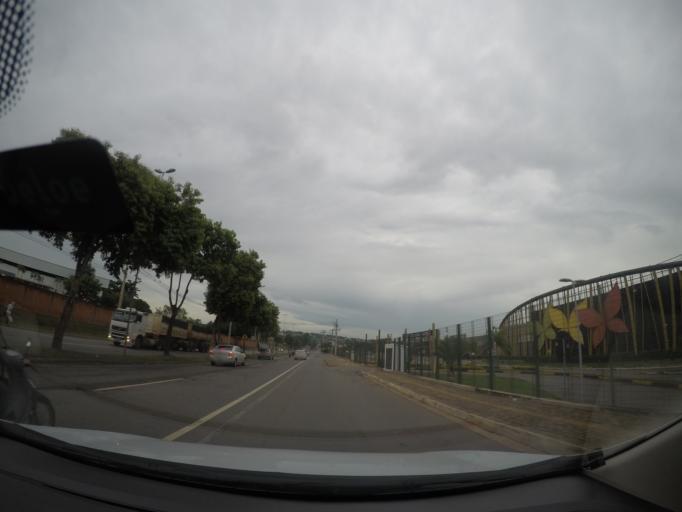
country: BR
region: Goias
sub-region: Goiania
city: Goiania
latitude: -16.6311
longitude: -49.2772
